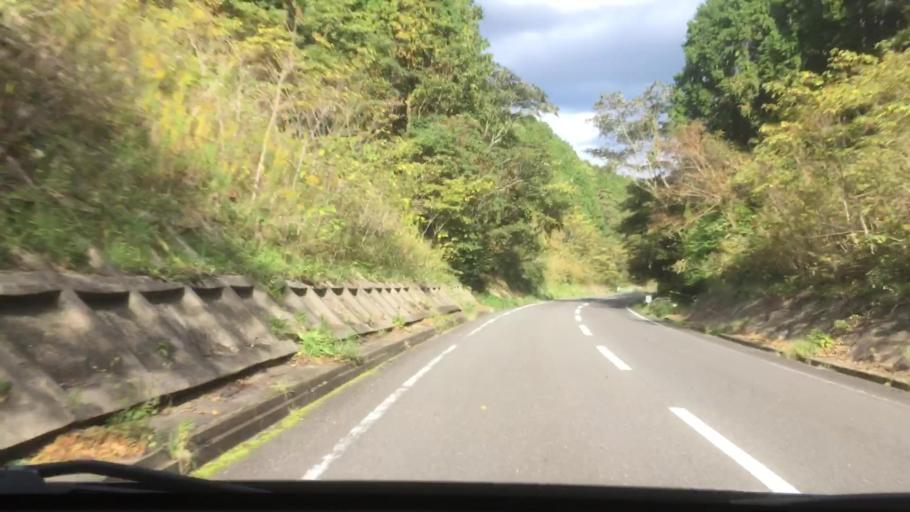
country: JP
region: Nagasaki
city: Sasebo
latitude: 33.0176
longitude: 129.7014
